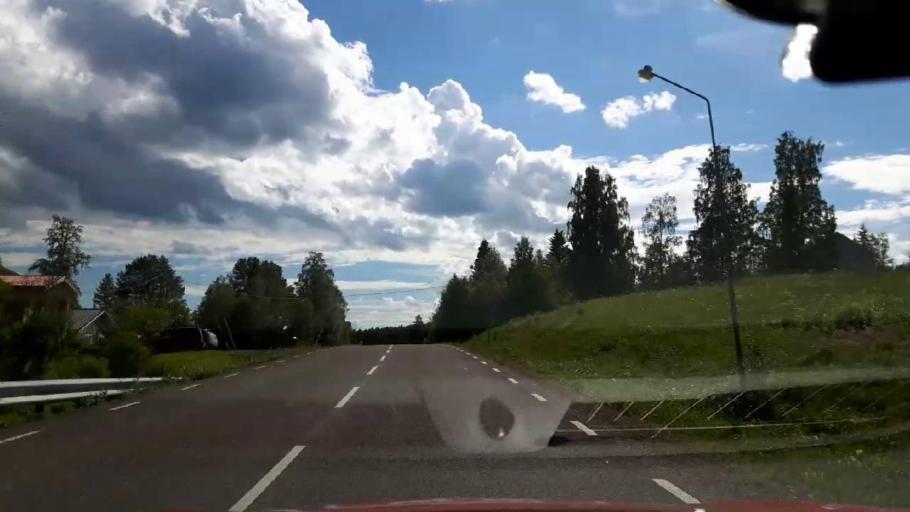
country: SE
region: Jaemtland
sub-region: Krokoms Kommun
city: Valla
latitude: 63.9864
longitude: 14.2259
